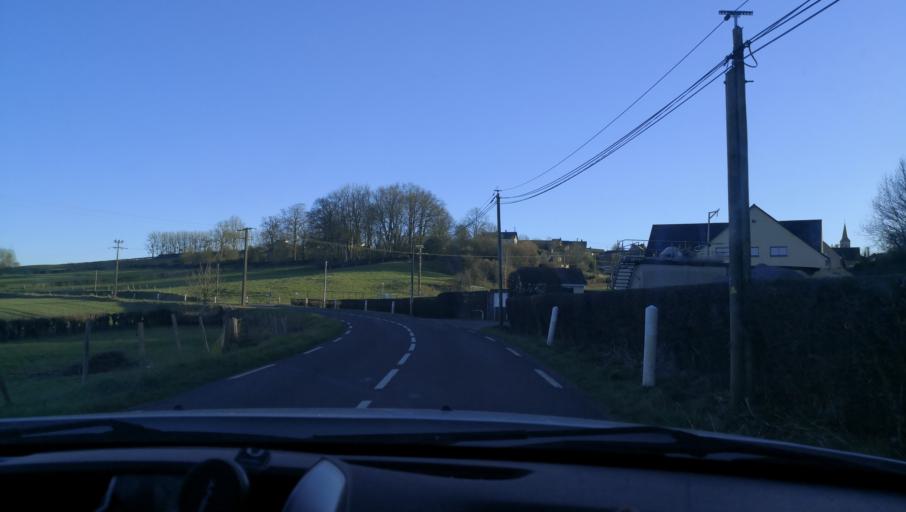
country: FR
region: Haute-Normandie
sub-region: Departement de la Seine-Maritime
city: Saint-Martin-Osmonville
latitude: 49.6428
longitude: 1.3030
